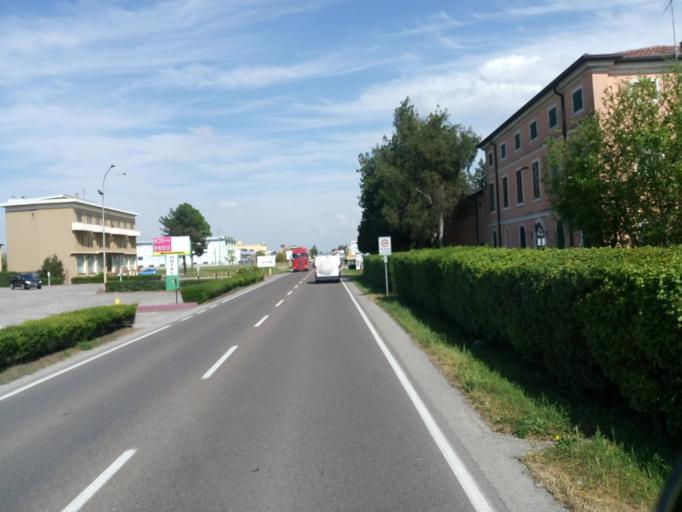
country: IT
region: Veneto
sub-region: Provincia di Verona
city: Casaleone
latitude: 45.1792
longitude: 11.1700
